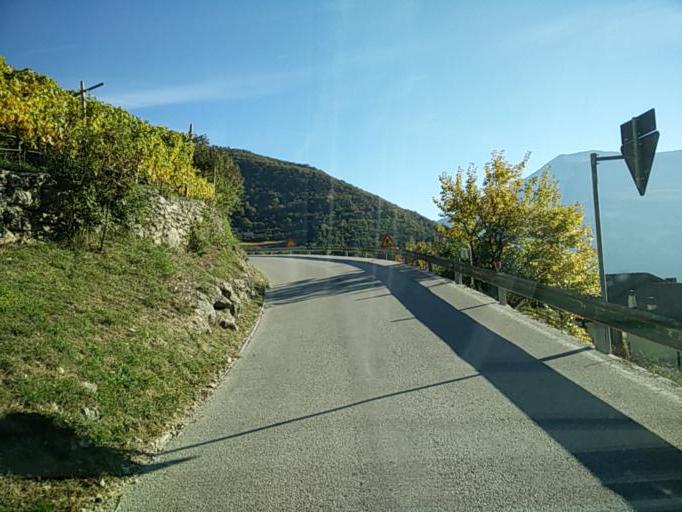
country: IT
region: Trentino-Alto Adige
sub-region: Provincia di Trento
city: Covelo
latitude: 45.9802
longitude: 11.0672
